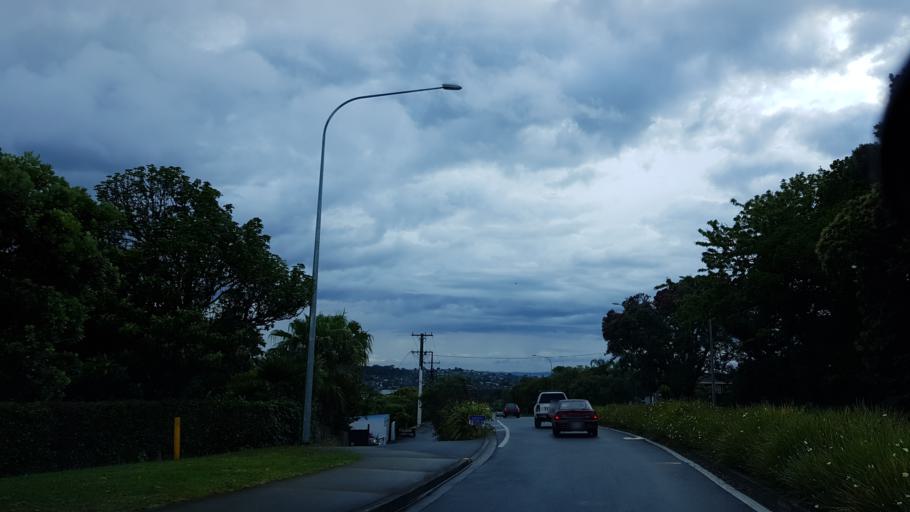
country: NZ
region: Auckland
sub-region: Auckland
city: North Shore
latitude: -36.7697
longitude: 174.7220
